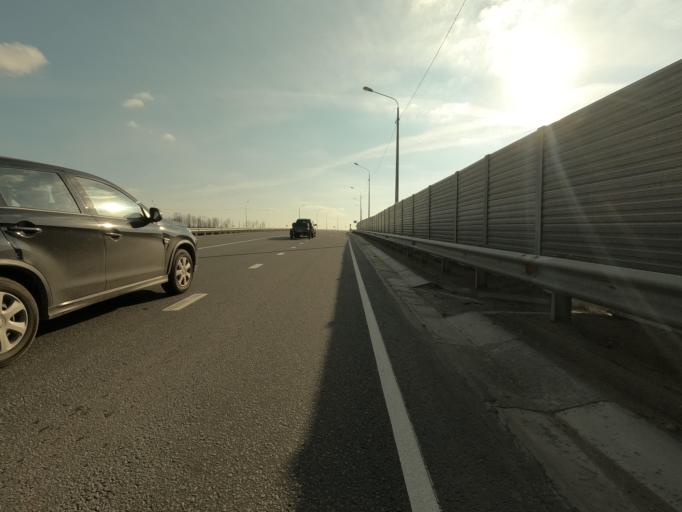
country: RU
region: Leningrad
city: Mga
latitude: 59.7592
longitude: 31.0936
